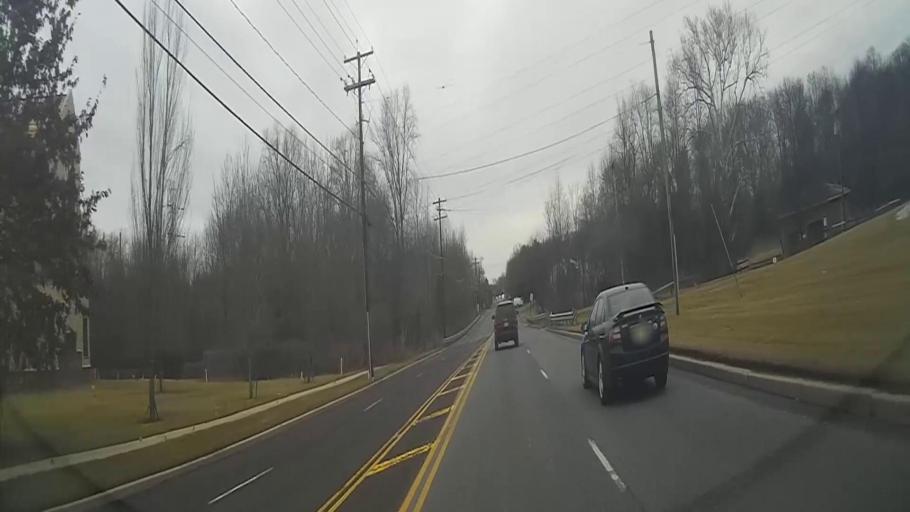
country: US
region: New Jersey
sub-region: Burlington County
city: Marlton
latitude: 39.8726
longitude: -74.9311
